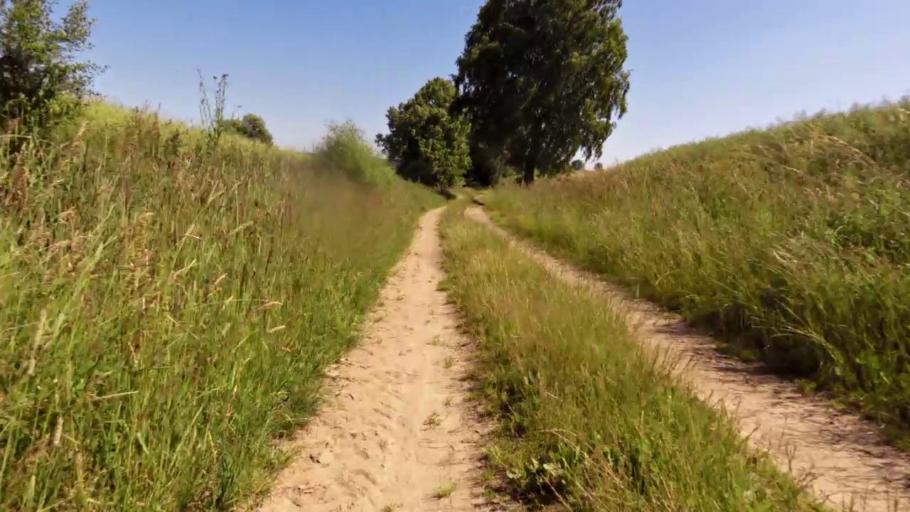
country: PL
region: West Pomeranian Voivodeship
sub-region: Powiat swidwinski
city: Rabino
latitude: 53.8515
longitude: 16.0083
